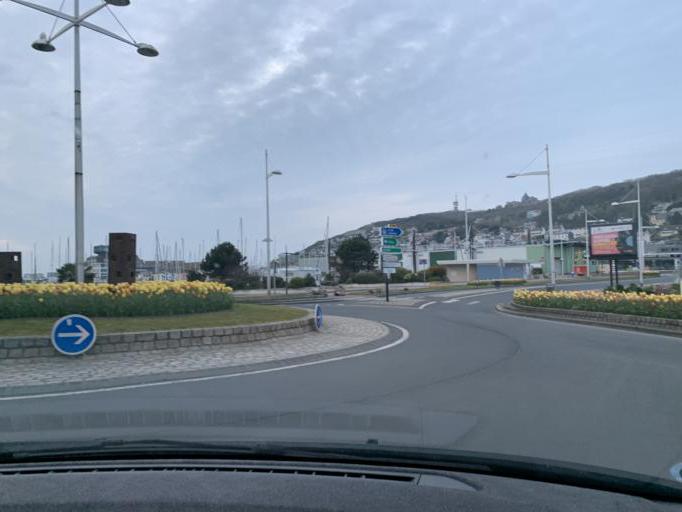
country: FR
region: Haute-Normandie
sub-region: Departement de la Seine-Maritime
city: Fecamp
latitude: 49.7593
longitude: 0.3733
